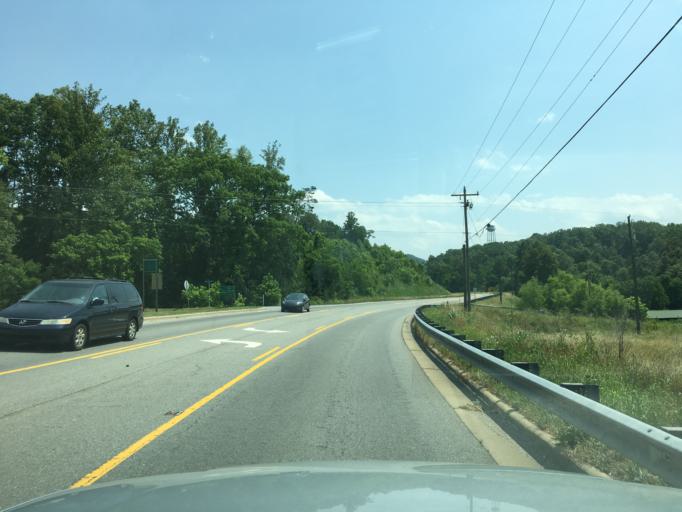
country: US
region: North Carolina
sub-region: McDowell County
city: Marion
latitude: 35.6510
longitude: -81.9548
